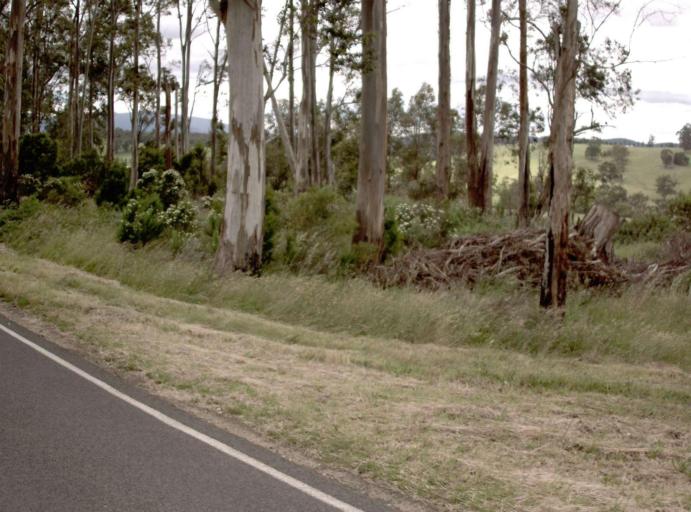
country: AU
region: Victoria
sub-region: Latrobe
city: Moe
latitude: -38.0418
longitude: 146.1671
